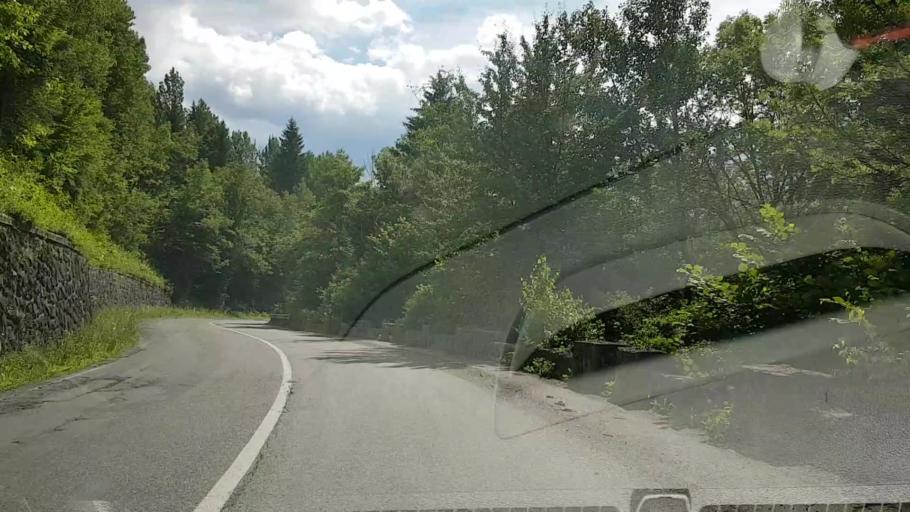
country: RO
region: Neamt
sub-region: Comuna Poiana Teiului
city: Poiana Teiului
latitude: 47.0778
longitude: 25.9663
